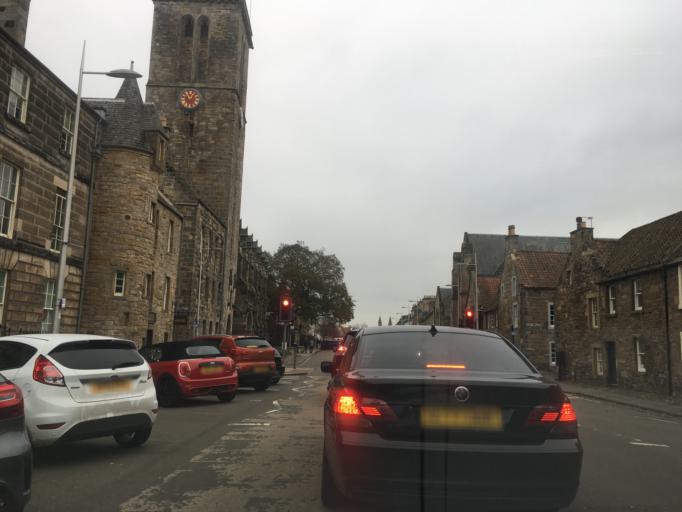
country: GB
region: Scotland
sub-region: Fife
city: Saint Andrews
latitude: 56.3414
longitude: -2.7957
